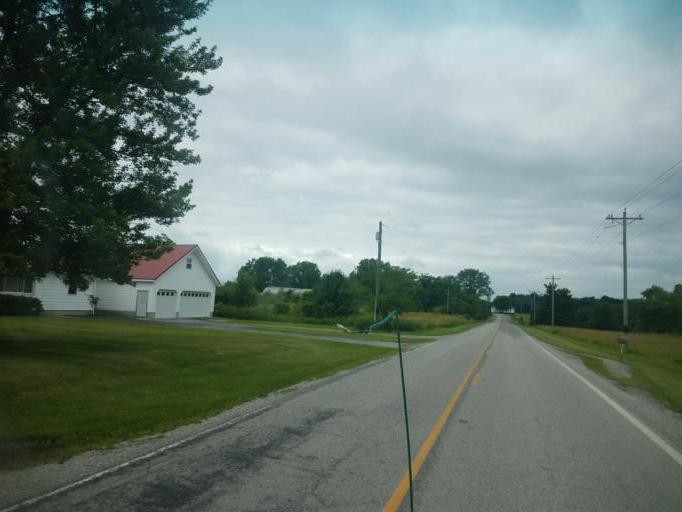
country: US
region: Ohio
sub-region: Champaign County
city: North Lewisburg
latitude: 40.4121
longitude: -83.5044
